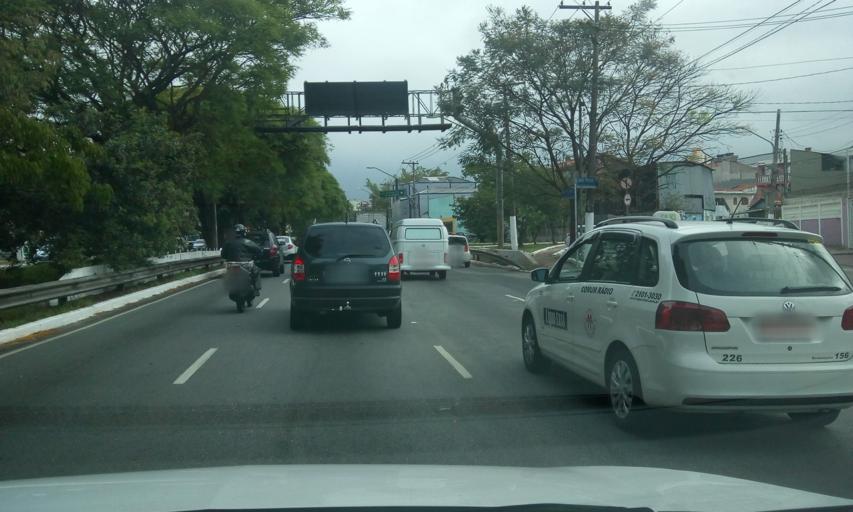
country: BR
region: Sao Paulo
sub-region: Sao Caetano Do Sul
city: Sao Caetano do Sul
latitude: -23.6207
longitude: -46.6115
